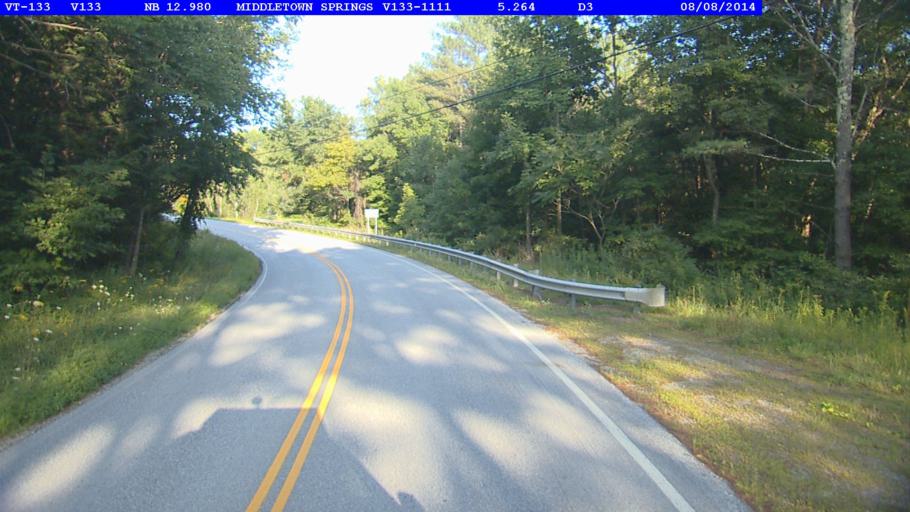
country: US
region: Vermont
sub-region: Rutland County
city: West Rutland
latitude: 43.4817
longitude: -73.0897
